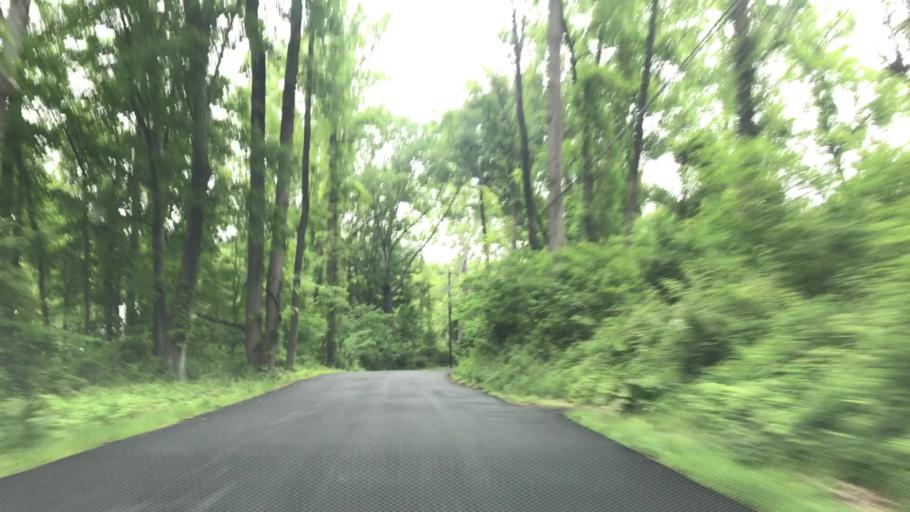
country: US
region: New Jersey
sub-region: Hunterdon County
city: Lebanon
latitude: 40.6629
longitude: -74.8340
